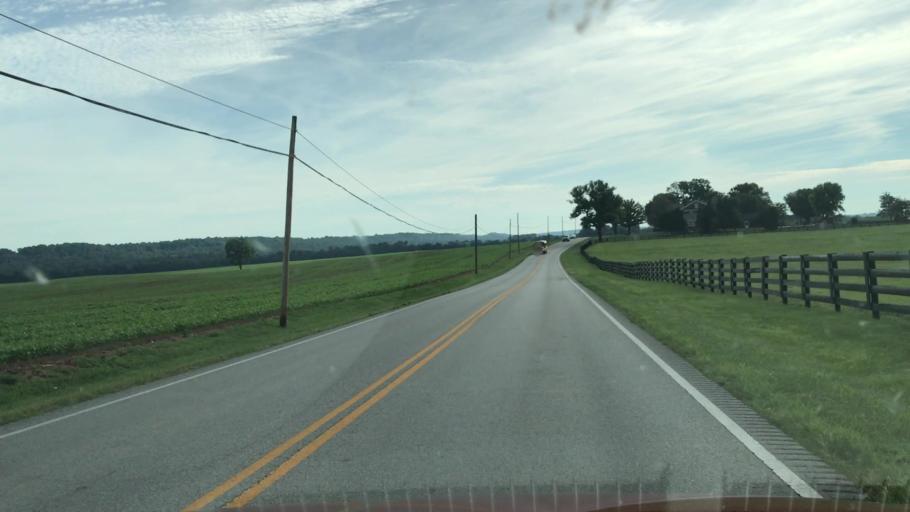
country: US
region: Kentucky
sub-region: Edmonson County
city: Brownsville
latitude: 37.0606
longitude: -86.2924
